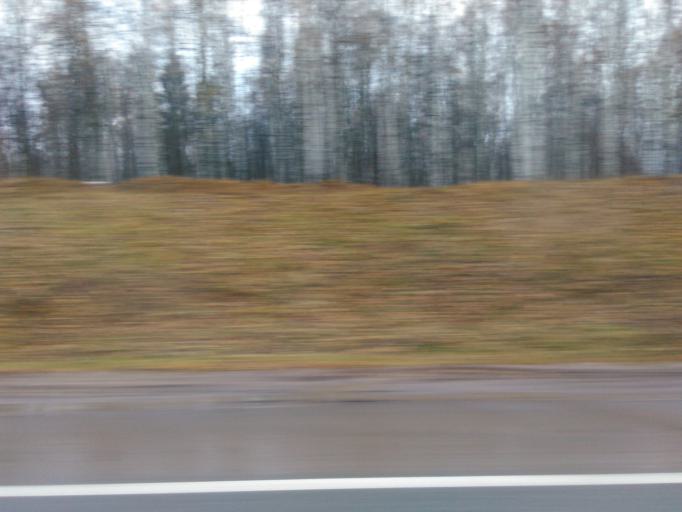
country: RU
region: Tatarstan
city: Osinovo
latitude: 55.8342
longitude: 48.8501
